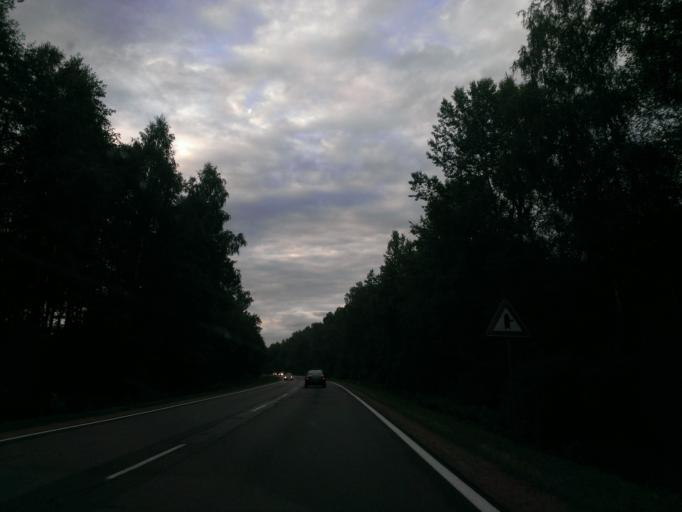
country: LV
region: Salaspils
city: Salaspils
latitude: 56.9092
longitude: 24.4053
